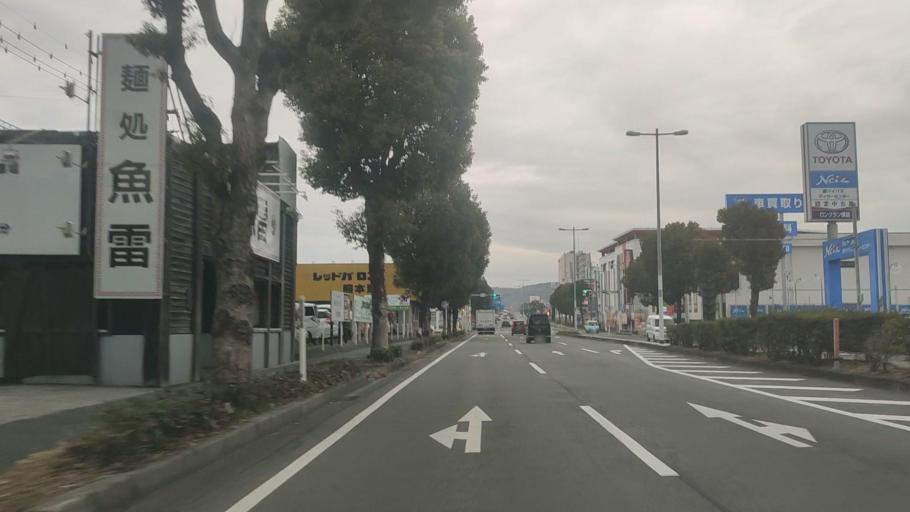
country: JP
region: Kumamoto
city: Kumamoto
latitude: 32.8272
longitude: 130.7668
